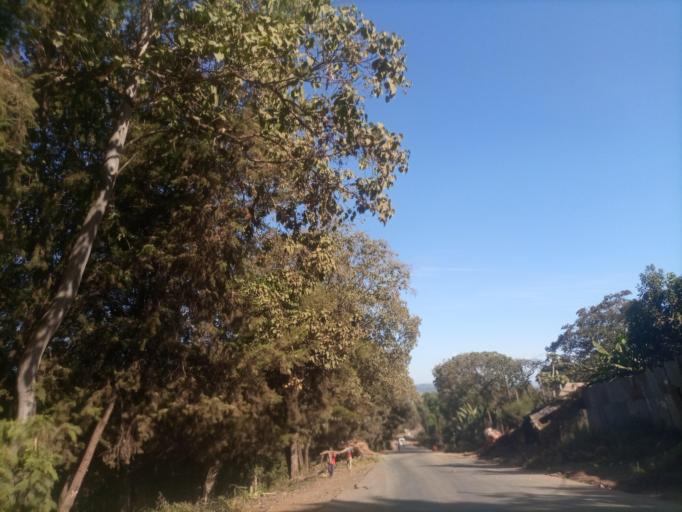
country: ET
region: Oromiya
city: Jima
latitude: 7.7005
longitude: 36.8108
